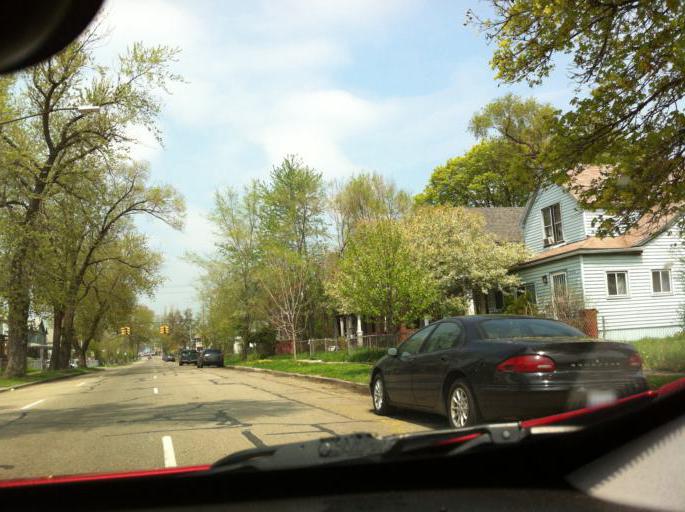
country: US
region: Michigan
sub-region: Wayne County
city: River Rouge
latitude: 42.3117
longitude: -83.1056
